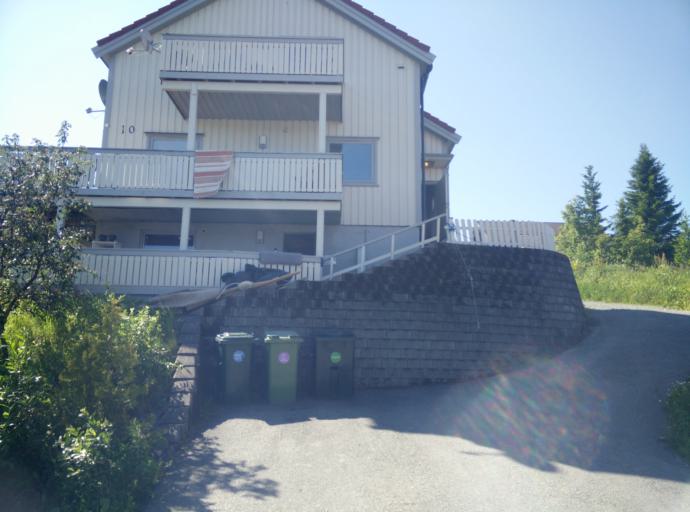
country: NO
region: Sor-Trondelag
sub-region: Trondheim
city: Trondheim
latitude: 63.4129
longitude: 10.3713
